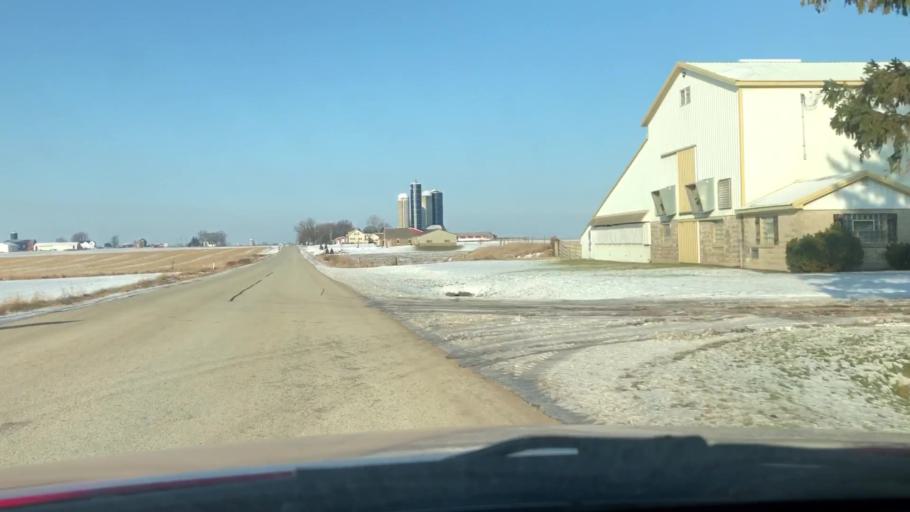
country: US
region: Wisconsin
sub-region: Outagamie County
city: Seymour
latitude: 44.4918
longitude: -88.3090
